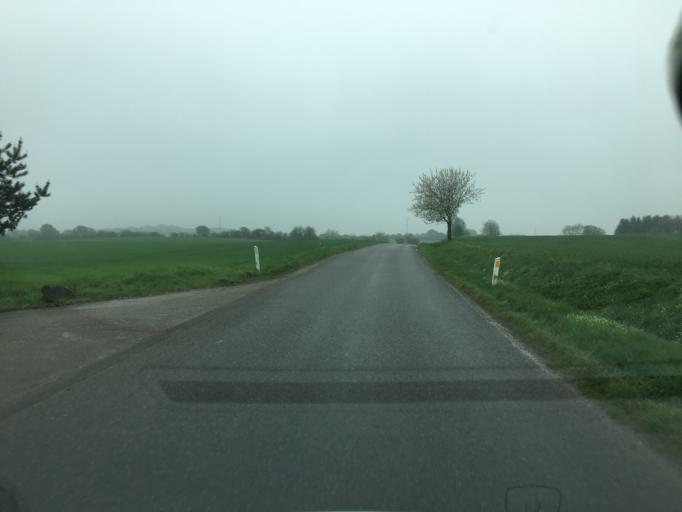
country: DK
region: South Denmark
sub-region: Haderslev Kommune
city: Haderslev
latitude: 55.2790
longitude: 9.4489
